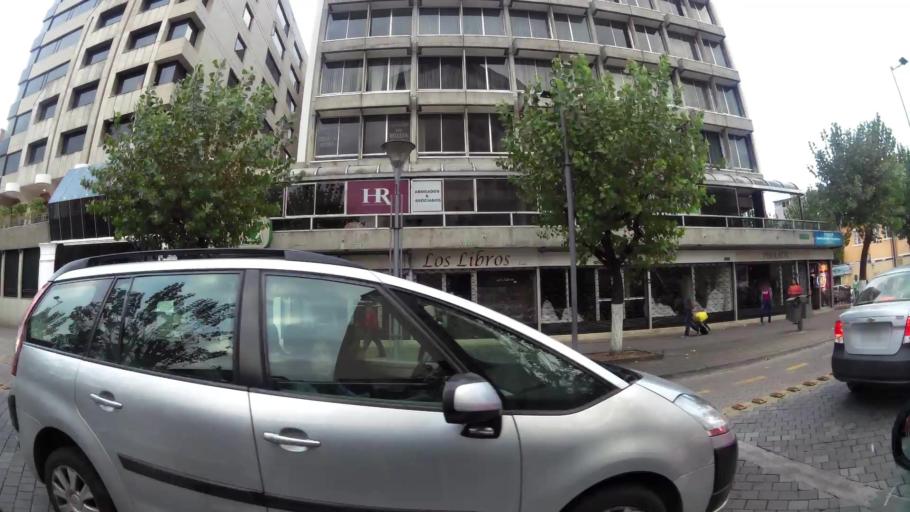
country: EC
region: Pichincha
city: Quito
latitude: -0.2024
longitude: -78.4937
